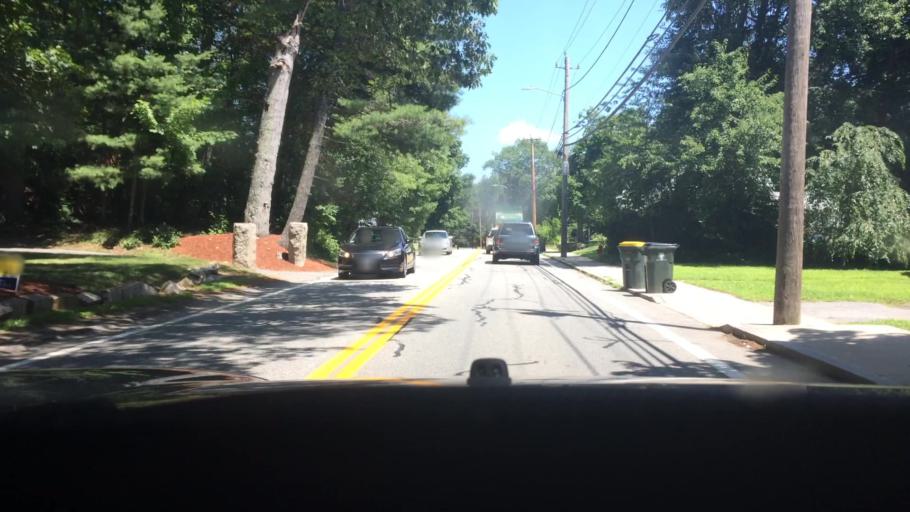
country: US
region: Rhode Island
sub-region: Providence County
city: Harrisville
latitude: 41.9661
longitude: -71.6691
